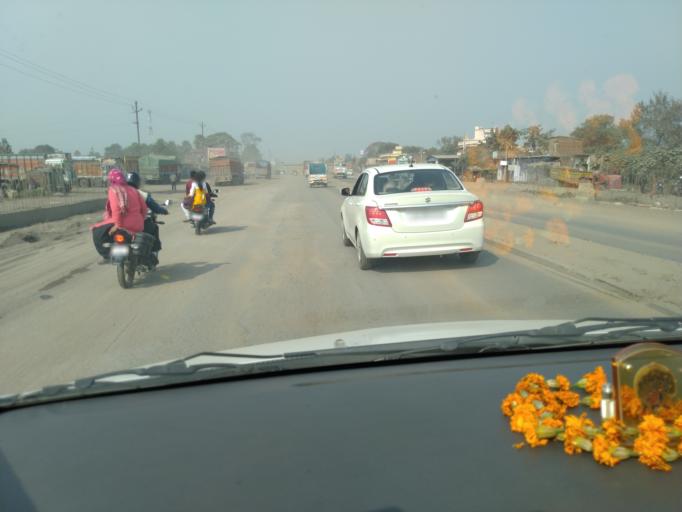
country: IN
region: Bihar
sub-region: Rohtas
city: Dehri
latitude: 24.9142
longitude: 84.1610
